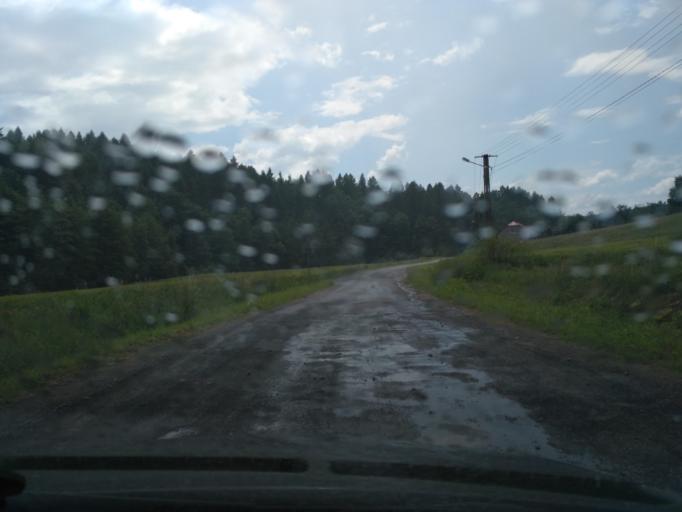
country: PL
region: Subcarpathian Voivodeship
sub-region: Powiat przeworski
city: Jawornik Polski
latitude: 49.9342
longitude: 22.2827
